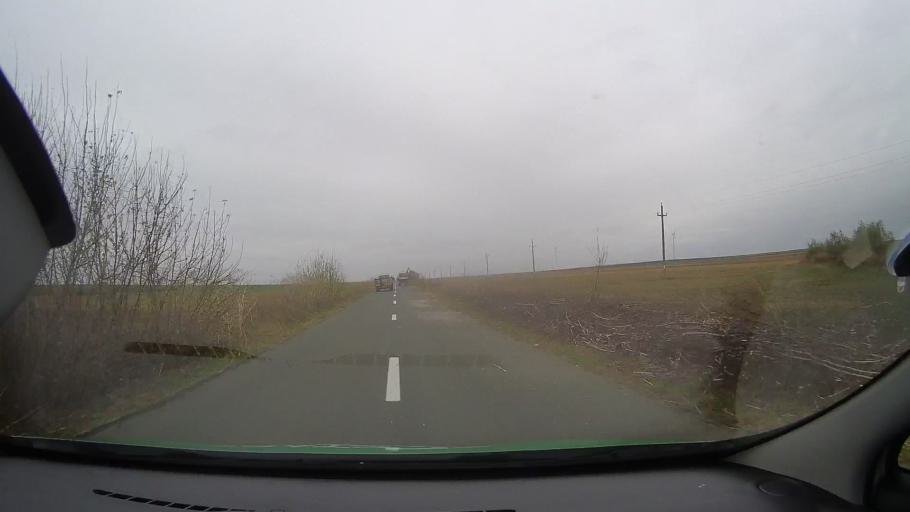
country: RO
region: Constanta
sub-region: Comuna Targusor
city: Targusor
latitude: 44.4696
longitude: 28.3892
